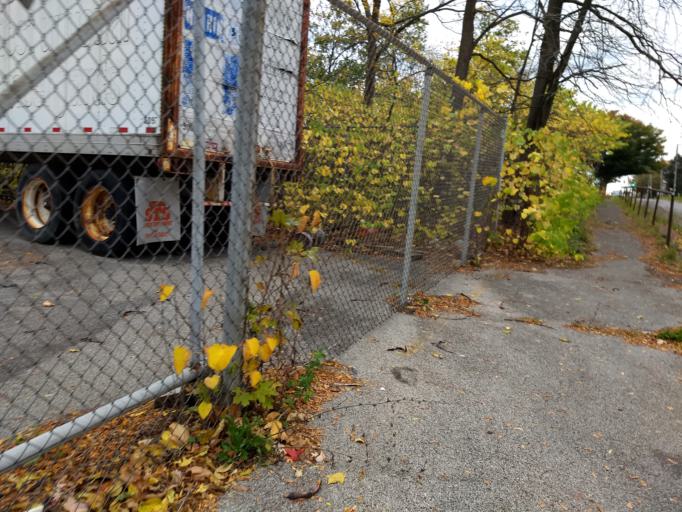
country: US
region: New York
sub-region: Onondaga County
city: Mattydale
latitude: 43.0812
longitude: -76.1552
